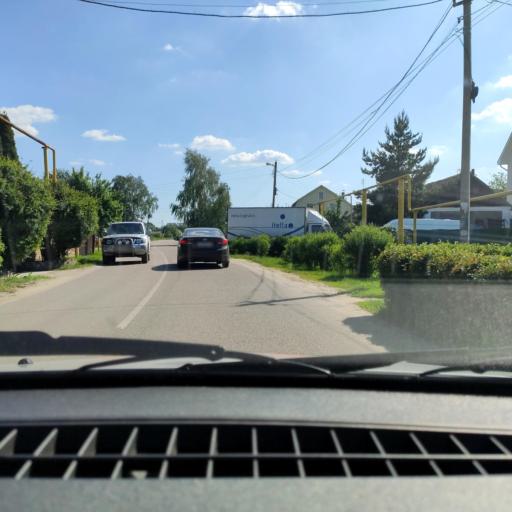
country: RU
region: Voronezj
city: Ramon'
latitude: 51.8171
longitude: 39.2650
